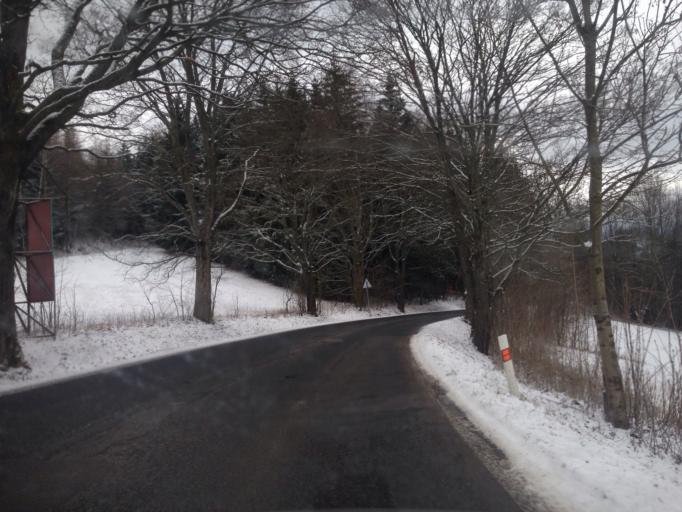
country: CZ
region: Liberecky
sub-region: Okres Semily
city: Vysoke nad Jizerou
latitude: 50.6937
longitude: 15.3906
